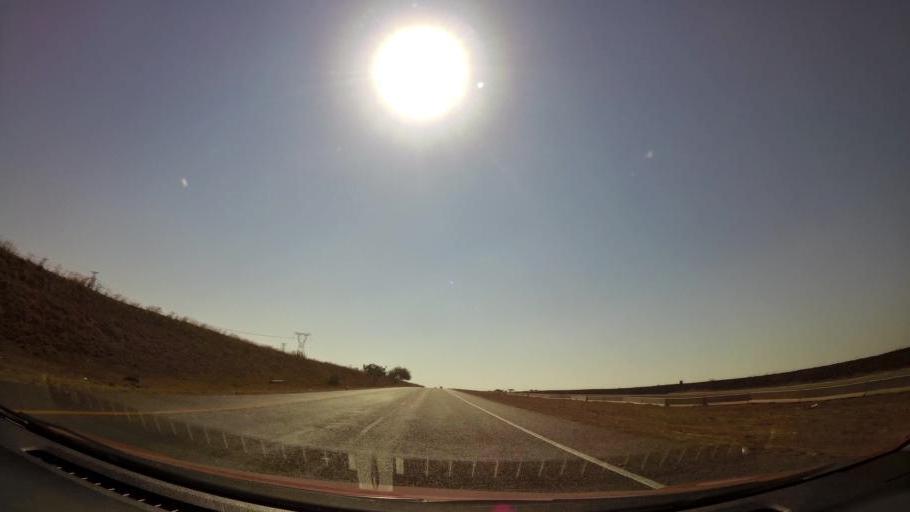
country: ZA
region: Gauteng
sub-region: City of Tshwane Metropolitan Municipality
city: Mabopane
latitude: -25.5482
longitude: 28.1100
